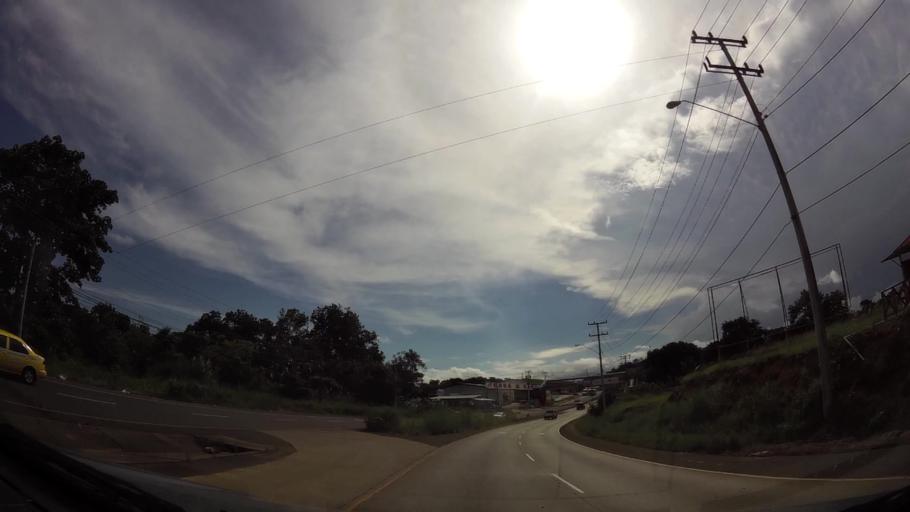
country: PA
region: Panama
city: La Chorrera
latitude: 8.8960
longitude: -79.7593
